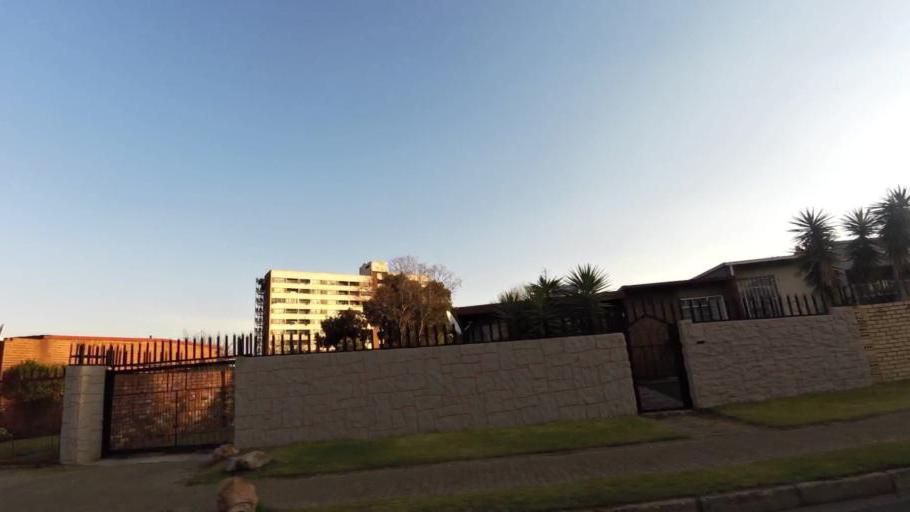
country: ZA
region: Gauteng
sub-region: City of Johannesburg Metropolitan Municipality
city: Johannesburg
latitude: -26.1809
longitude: 27.9620
